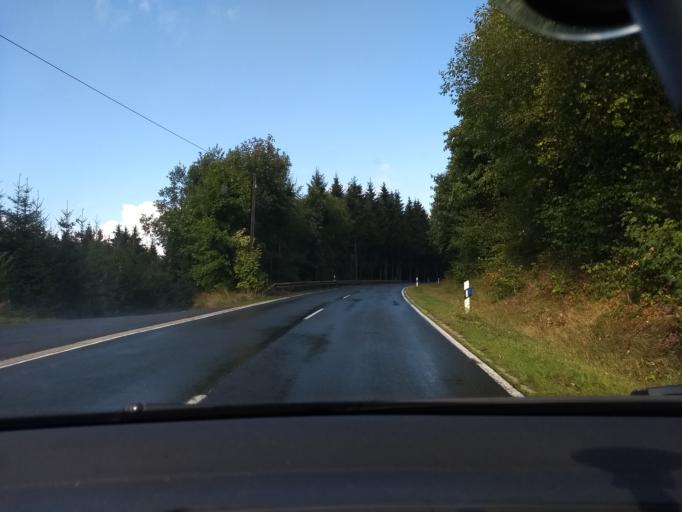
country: DE
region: North Rhine-Westphalia
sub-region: Regierungsbezirk Arnsberg
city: Finnentrop
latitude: 51.2178
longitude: 8.0204
